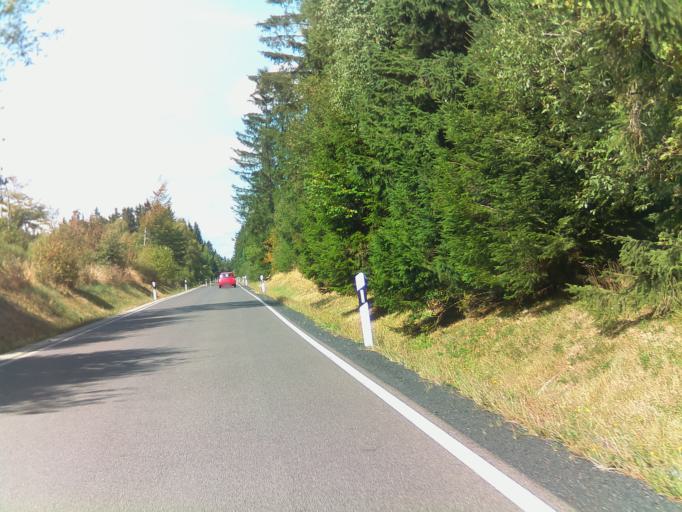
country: DE
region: Thuringia
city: Birx
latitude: 50.5150
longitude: 10.0732
